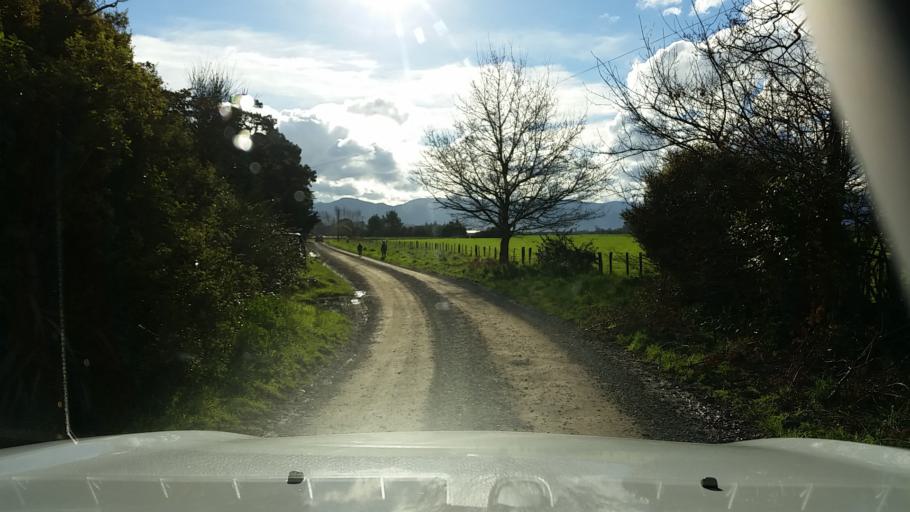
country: NZ
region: Wellington
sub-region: South Wairarapa District
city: Waipawa
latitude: -41.2311
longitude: 175.3235
